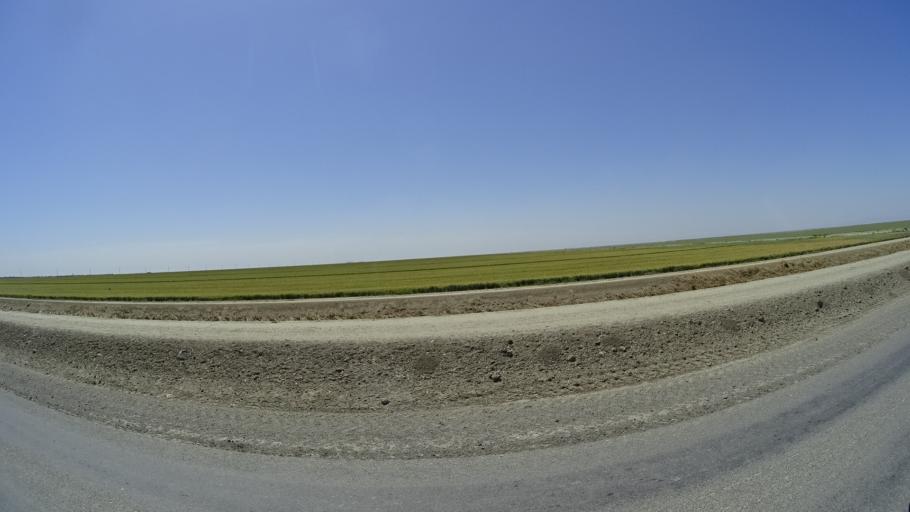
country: US
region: California
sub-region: Kings County
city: Corcoran
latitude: 36.0215
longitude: -119.5797
